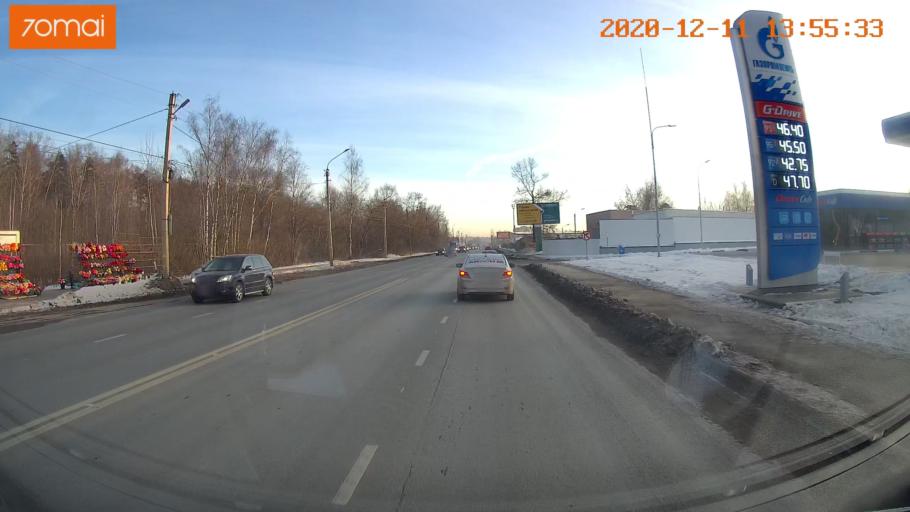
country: RU
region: Kostroma
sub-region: Kostromskoy Rayon
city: Kostroma
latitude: 57.7815
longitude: 40.9654
